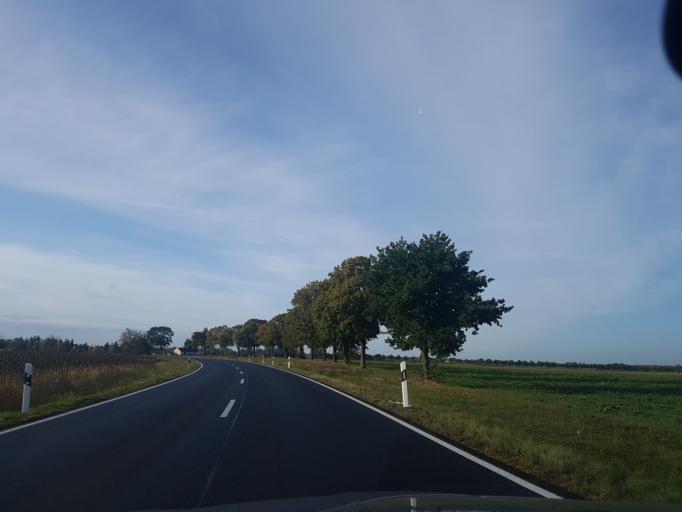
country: DE
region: Saxony
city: Arzberg
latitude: 51.6225
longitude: 13.1482
